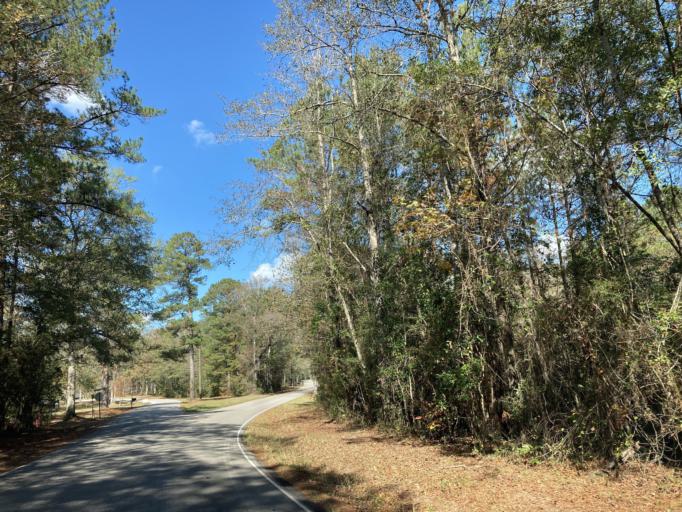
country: US
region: Mississippi
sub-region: Lamar County
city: Purvis
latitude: 31.2350
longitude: -89.4333
